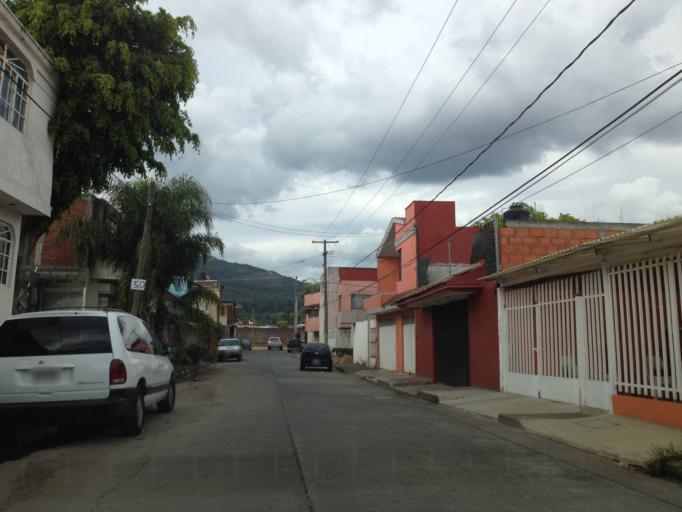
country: MX
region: Michoacan
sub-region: Uruapan
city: Uruapan
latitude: 19.4182
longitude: -102.0358
